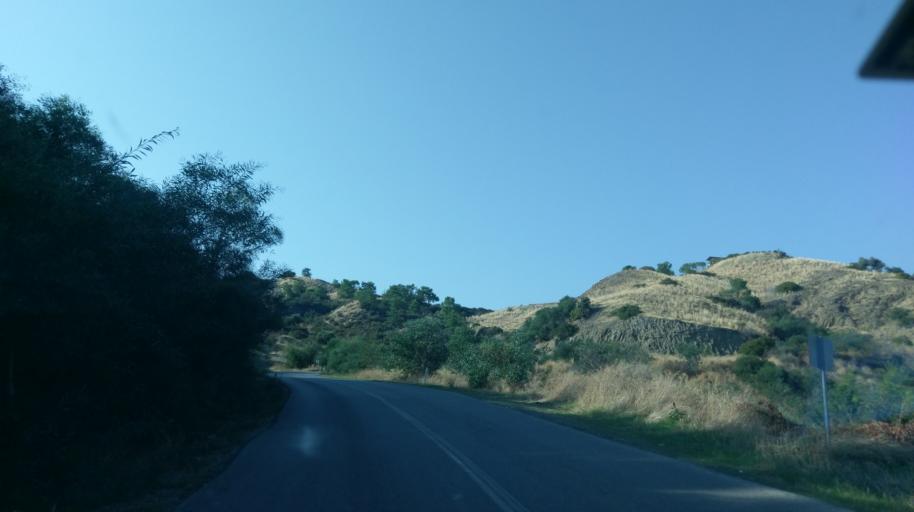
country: CY
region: Lefkosia
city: Kato Pyrgos
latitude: 35.1557
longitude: 32.7679
